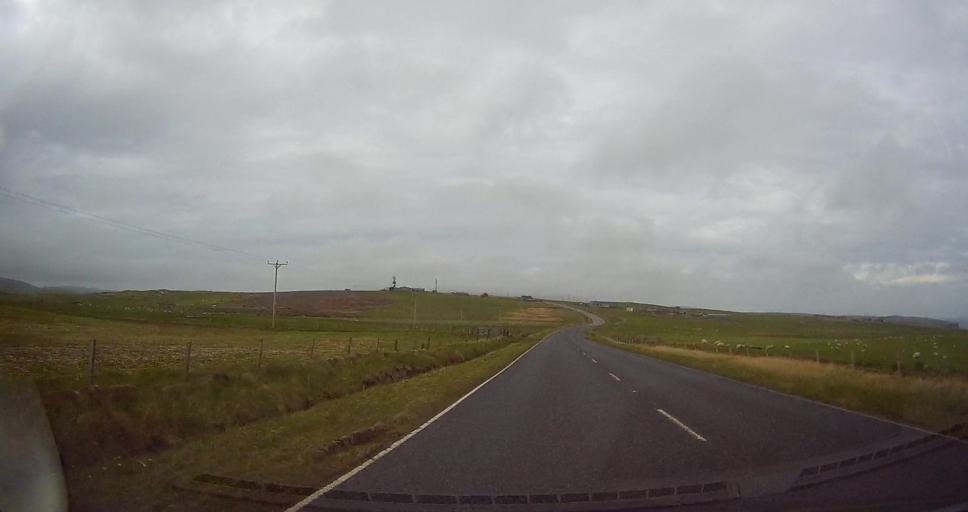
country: GB
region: Scotland
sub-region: Shetland Islands
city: Sandwick
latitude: 59.9053
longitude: -1.3026
